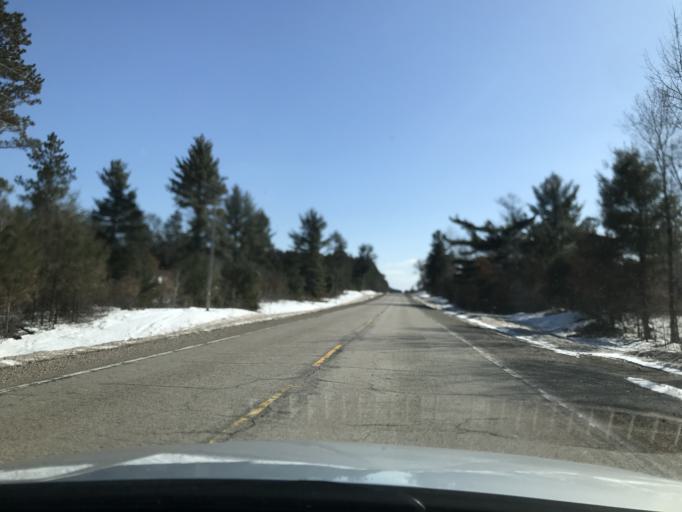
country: US
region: Wisconsin
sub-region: Marinette County
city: Niagara
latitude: 45.3875
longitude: -88.0997
